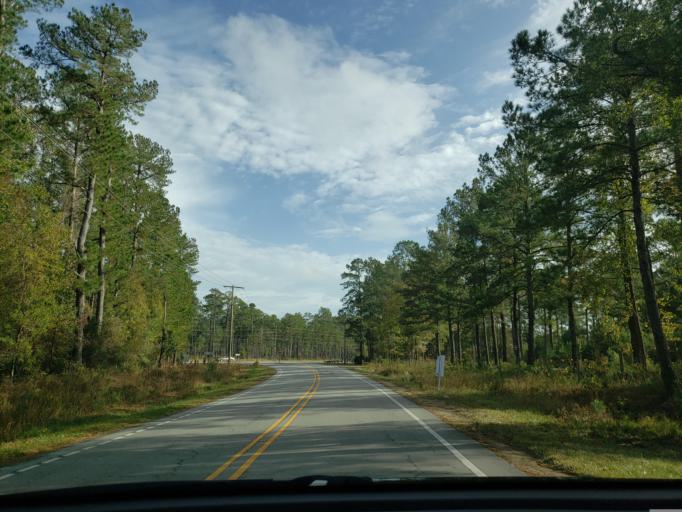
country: US
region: North Carolina
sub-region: Onslow County
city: Jacksonville
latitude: 34.6553
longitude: -77.4766
